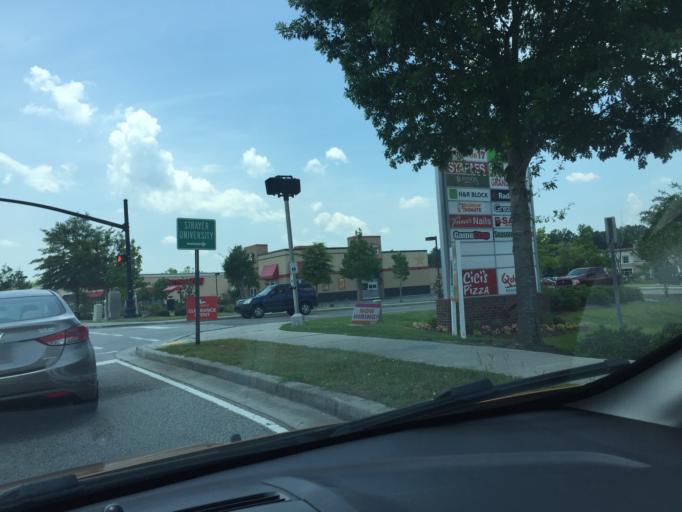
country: US
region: South Carolina
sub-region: Berkeley County
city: Hanahan
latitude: 32.8743
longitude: -80.0206
